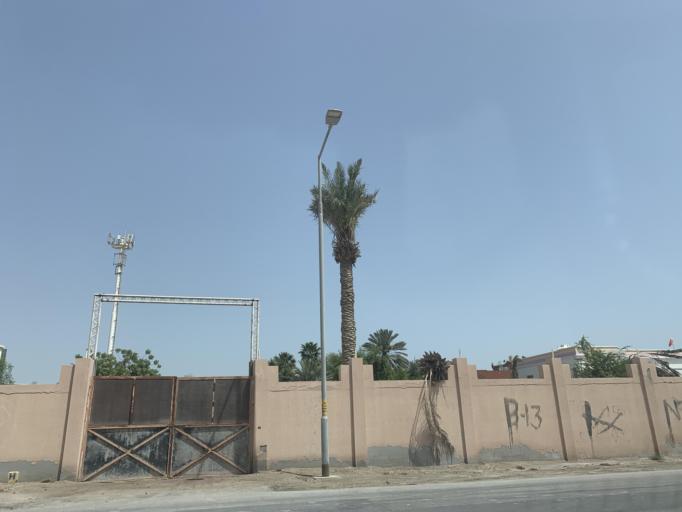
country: BH
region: Northern
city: Sitrah
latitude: 26.1560
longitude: 50.5827
